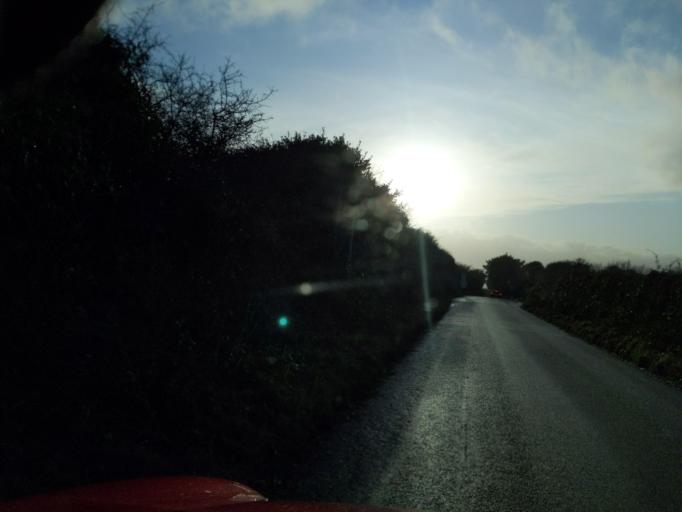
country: GB
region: England
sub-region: Cornwall
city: Fowey
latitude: 50.3281
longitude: -4.6243
